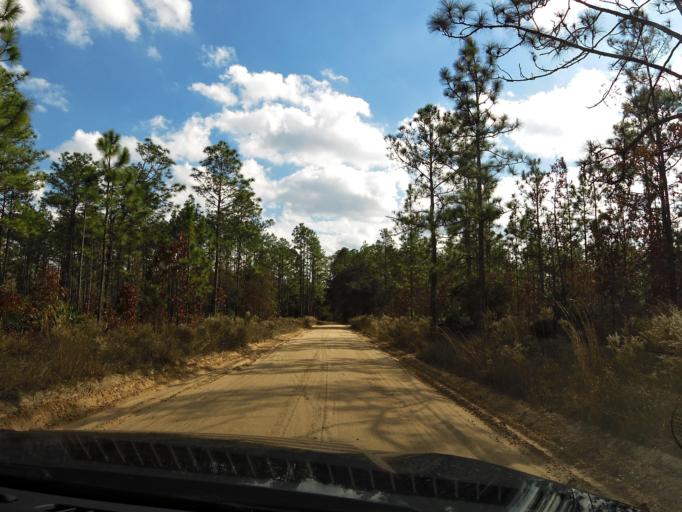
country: US
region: Florida
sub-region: Clay County
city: Middleburg
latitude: 30.1134
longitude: -81.9205
